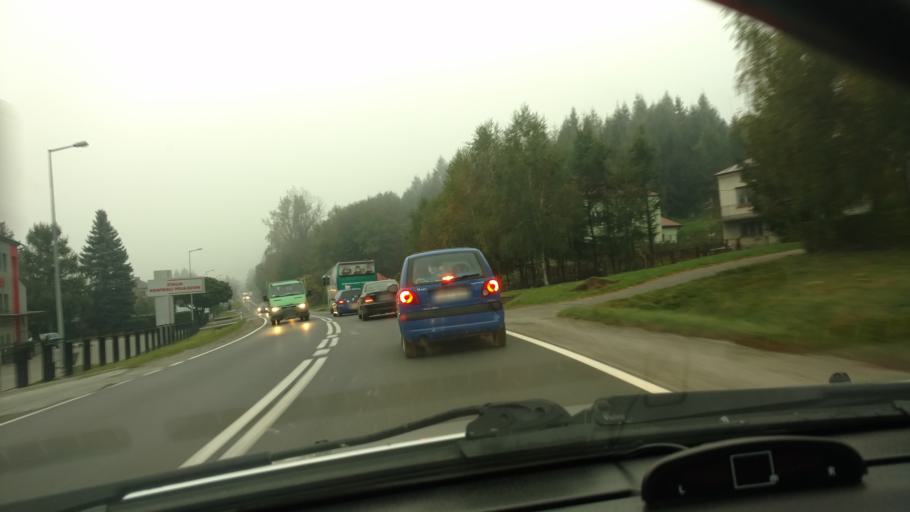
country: PL
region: Subcarpathian Voivodeship
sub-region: Powiat strzyzowski
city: Frysztak
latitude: 49.8395
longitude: 21.6096
